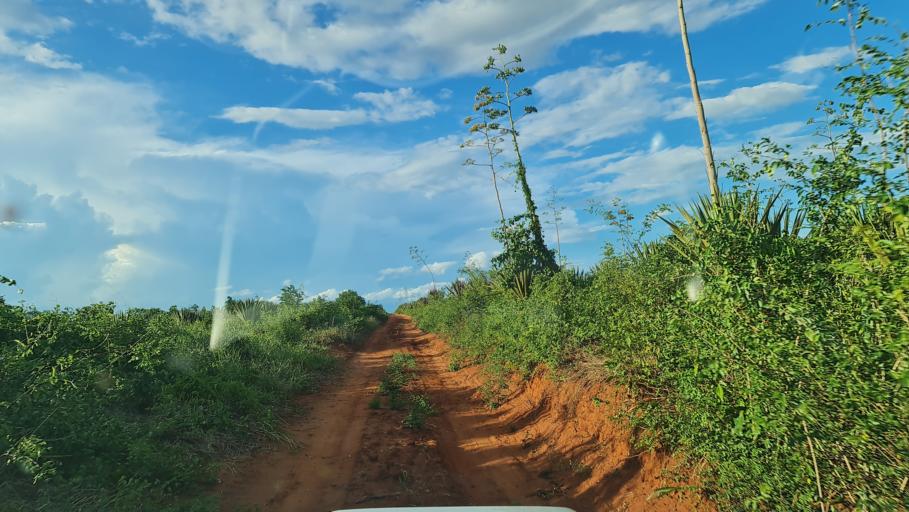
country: MZ
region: Nampula
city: Ilha de Mocambique
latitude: -14.9558
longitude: 40.1844
